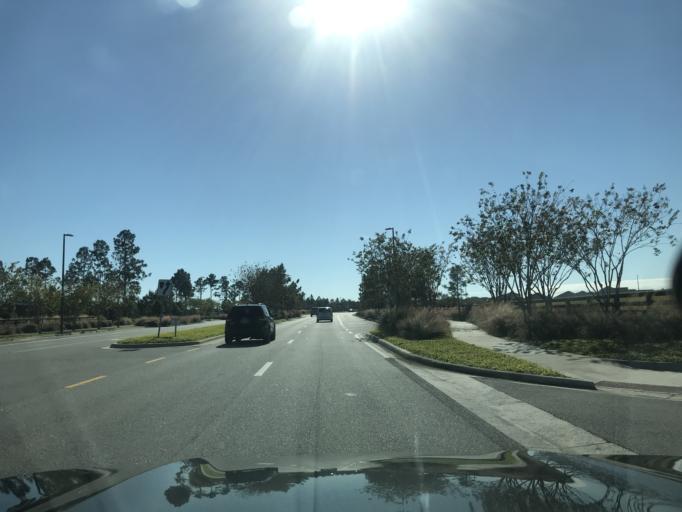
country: US
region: Florida
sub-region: Orange County
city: Oakland
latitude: 28.4622
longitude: -81.6256
